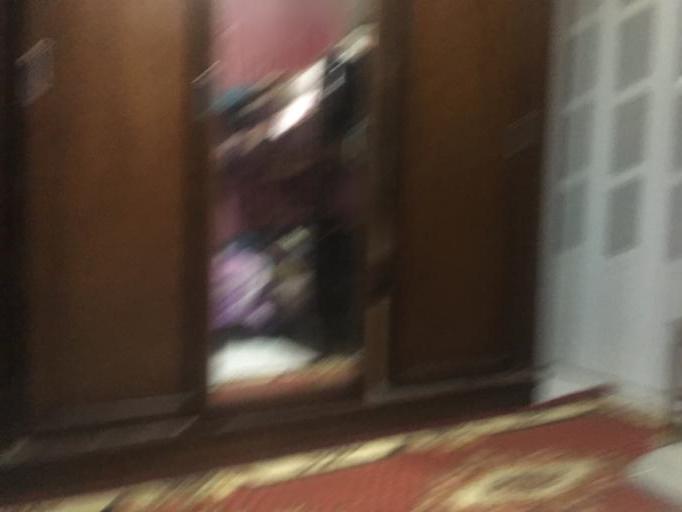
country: EG
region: Muhafazat al Qahirah
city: Cairo
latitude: 30.1084
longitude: 31.3077
